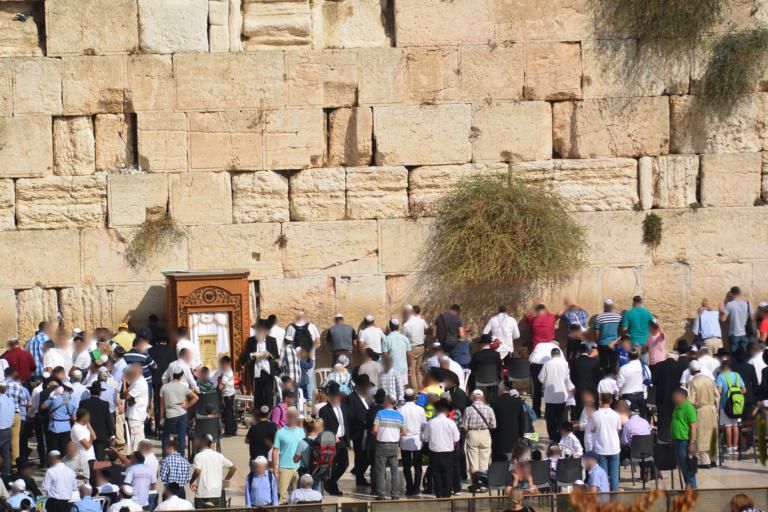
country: PS
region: West Bank
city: Old City
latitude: 31.7769
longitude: 35.2334
